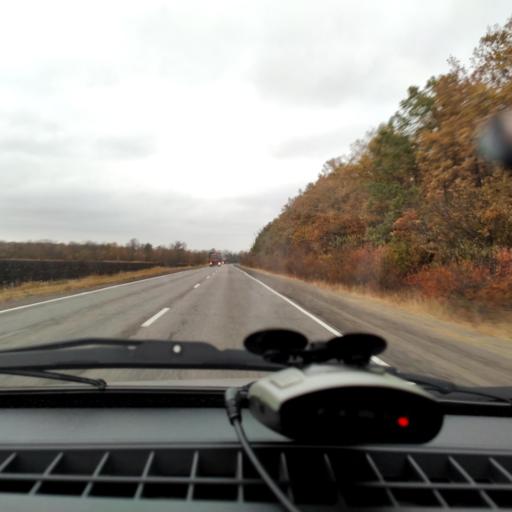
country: RU
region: Voronezj
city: Shilovo
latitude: 51.4009
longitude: 39.0028
